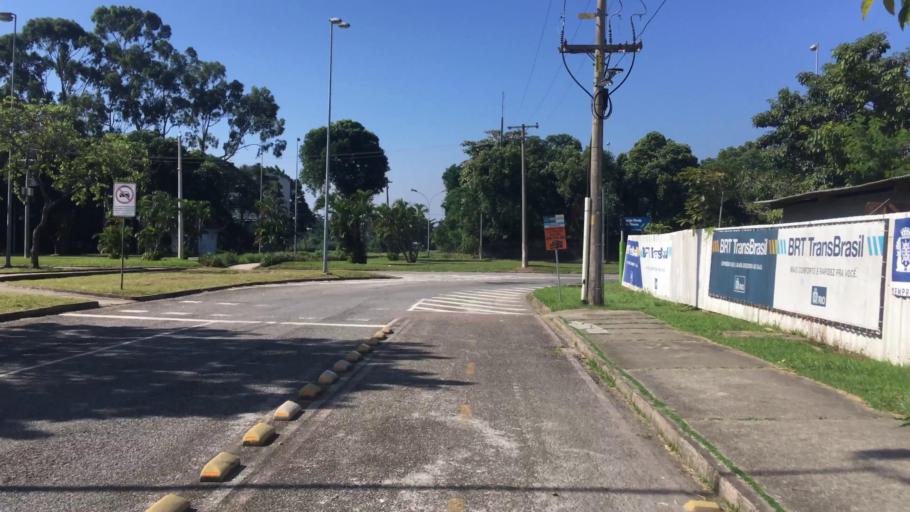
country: BR
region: Rio de Janeiro
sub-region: Rio De Janeiro
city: Rio de Janeiro
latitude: -22.8402
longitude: -43.2288
